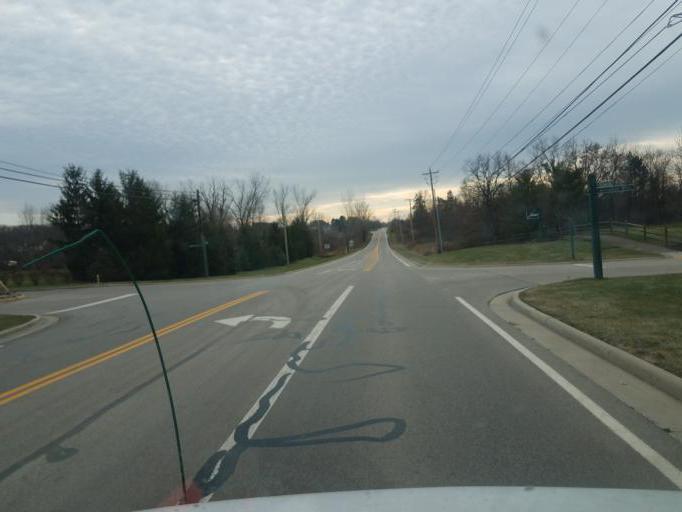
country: US
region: Ohio
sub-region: Delaware County
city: Lewis Center
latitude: 40.2112
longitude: -82.9862
